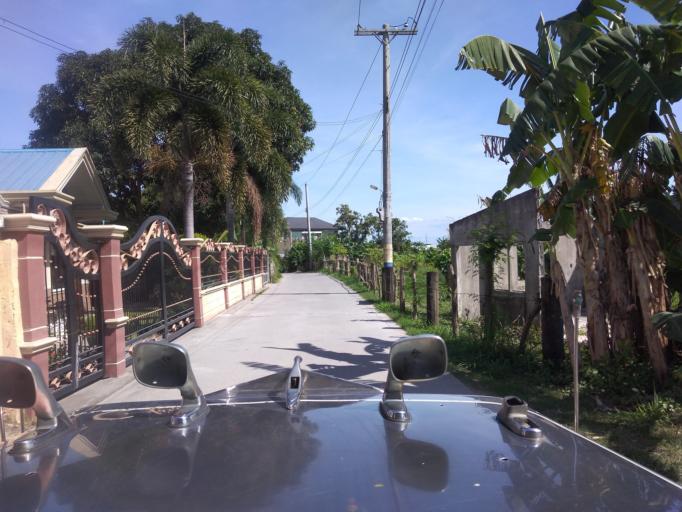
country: PH
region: Central Luzon
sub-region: Province of Pampanga
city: Magliman
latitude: 15.0264
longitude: 120.6532
